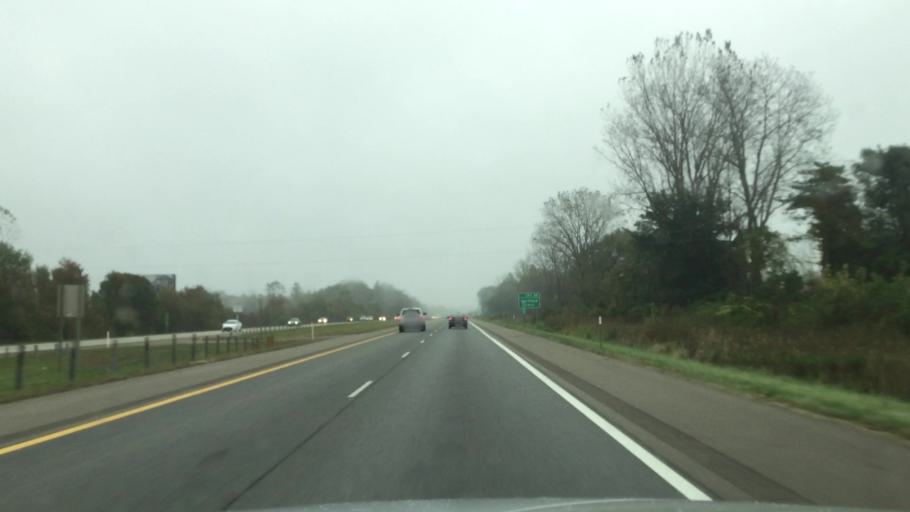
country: US
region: Michigan
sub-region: Van Buren County
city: Hartford
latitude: 42.1900
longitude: -86.1868
